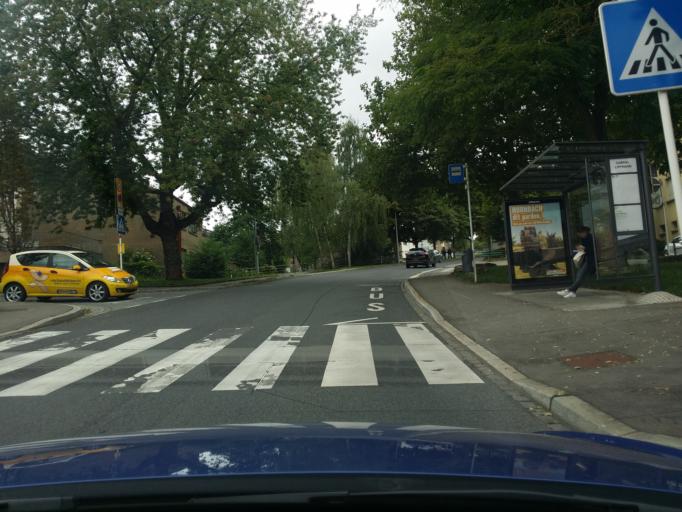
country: LU
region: Luxembourg
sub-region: Canton de Luxembourg
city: Luxembourg
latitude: 49.5992
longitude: 6.1427
